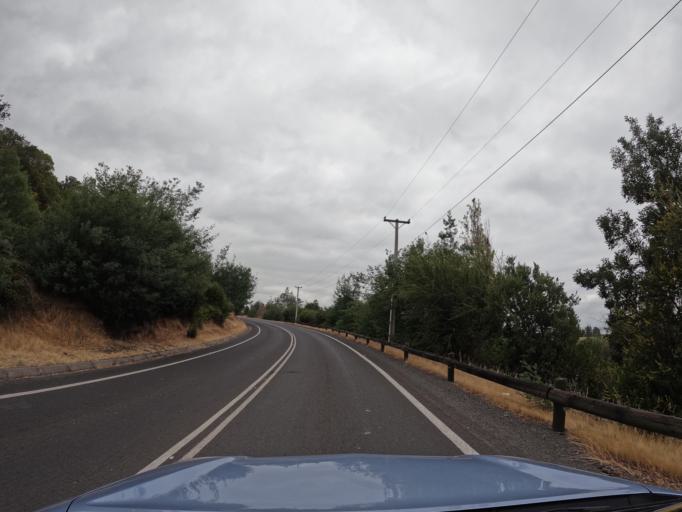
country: CL
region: O'Higgins
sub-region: Provincia de Colchagua
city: Chimbarongo
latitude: -34.7297
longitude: -71.0973
